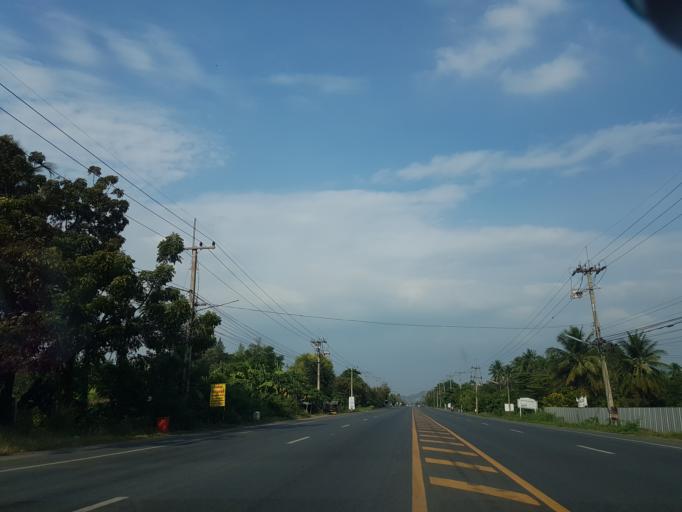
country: TH
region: Sara Buri
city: Ban Mo
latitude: 14.6335
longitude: 100.7523
